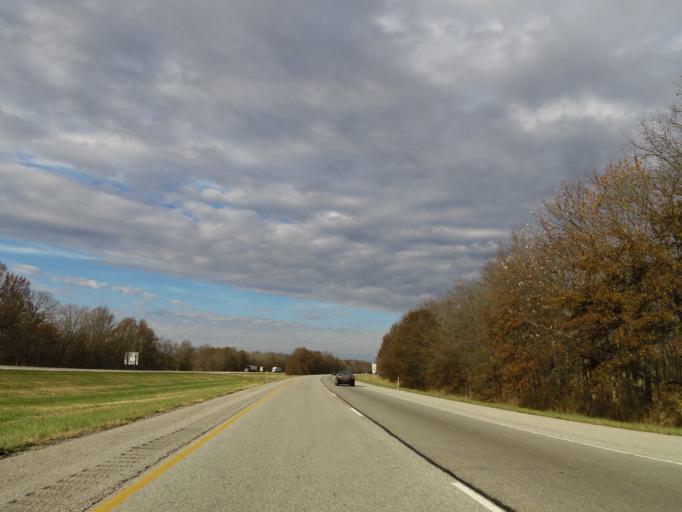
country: US
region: Illinois
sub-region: Washington County
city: Nashville
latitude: 38.3929
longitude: -89.3821
